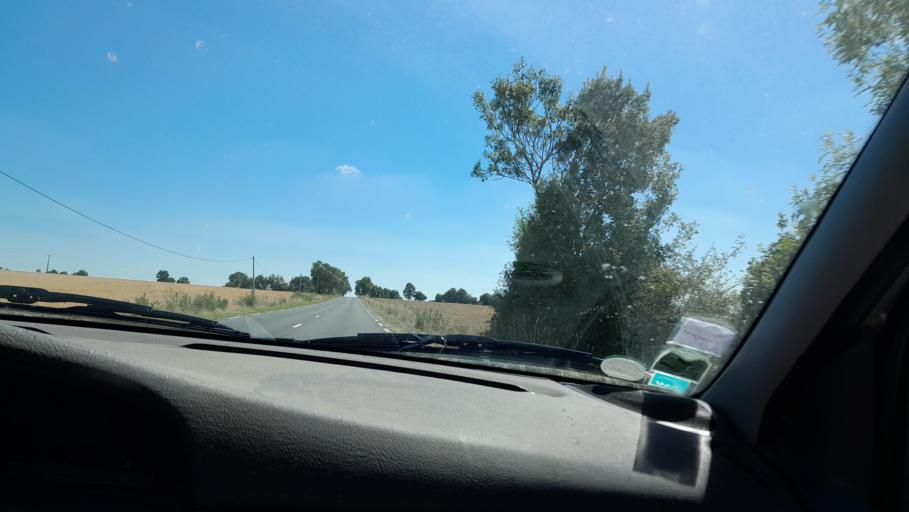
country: FR
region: Pays de la Loire
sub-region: Departement de la Loire-Atlantique
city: Saint-Mars-la-Jaille
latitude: 47.4774
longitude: -1.1743
